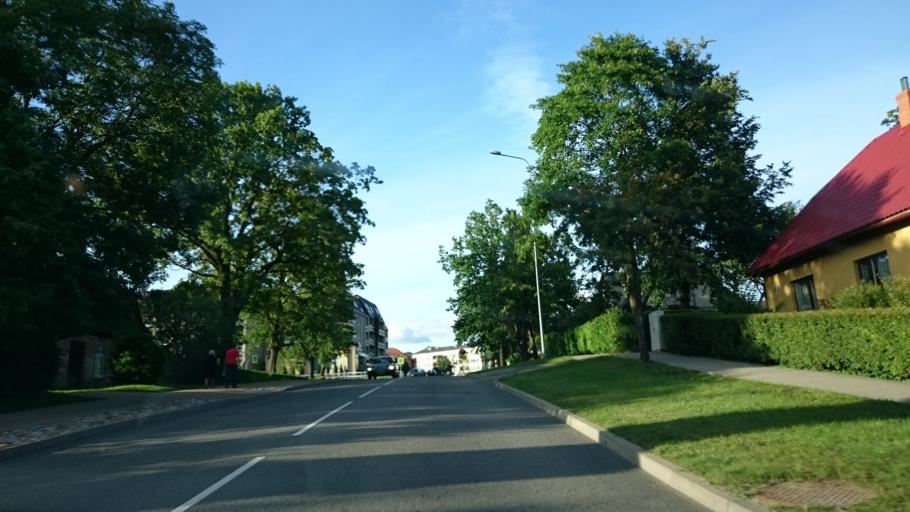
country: LV
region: Saldus Rajons
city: Saldus
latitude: 56.6649
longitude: 22.4799
